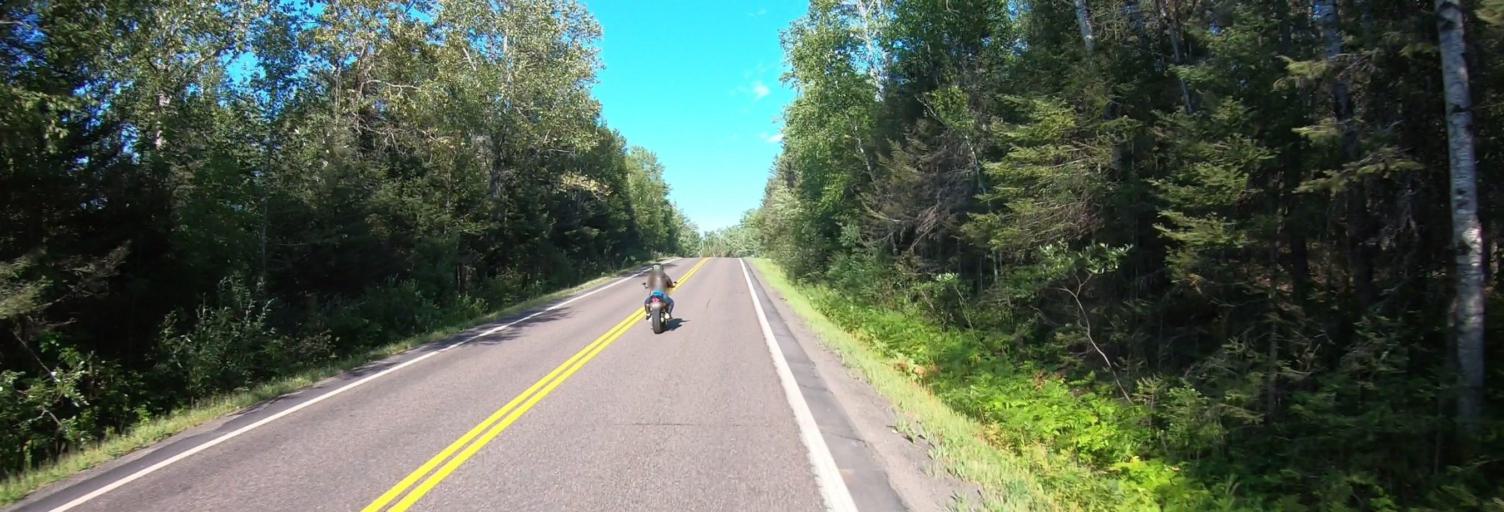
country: US
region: Minnesota
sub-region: Saint Louis County
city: Ely
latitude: 47.9465
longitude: -91.6541
